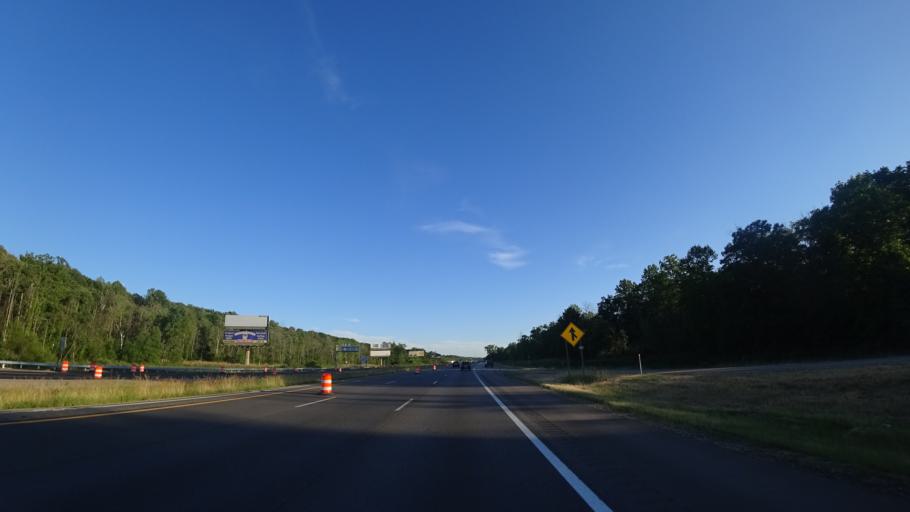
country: US
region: Michigan
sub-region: Berrien County
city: Stevensville
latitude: 42.0084
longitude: -86.5334
